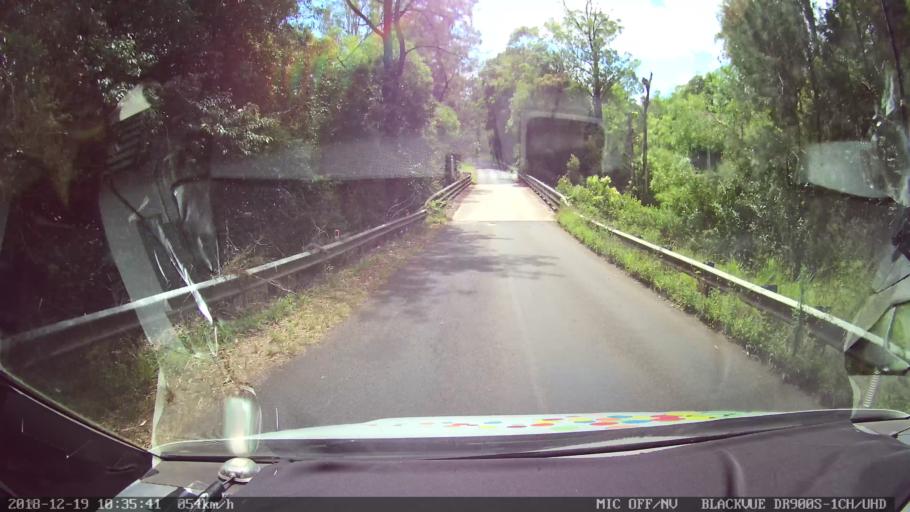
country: AU
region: New South Wales
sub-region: Lismore Municipality
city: Larnook
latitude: -28.5749
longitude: 153.1376
